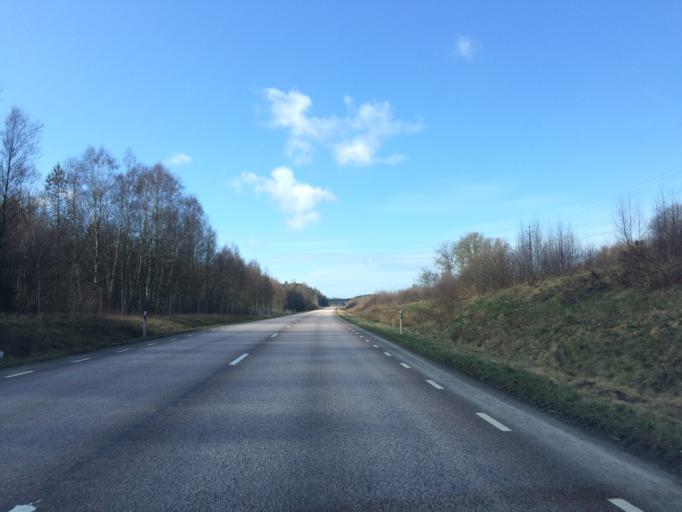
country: SE
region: Halland
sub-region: Laholms Kommun
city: Knared
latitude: 56.5180
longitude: 13.2920
